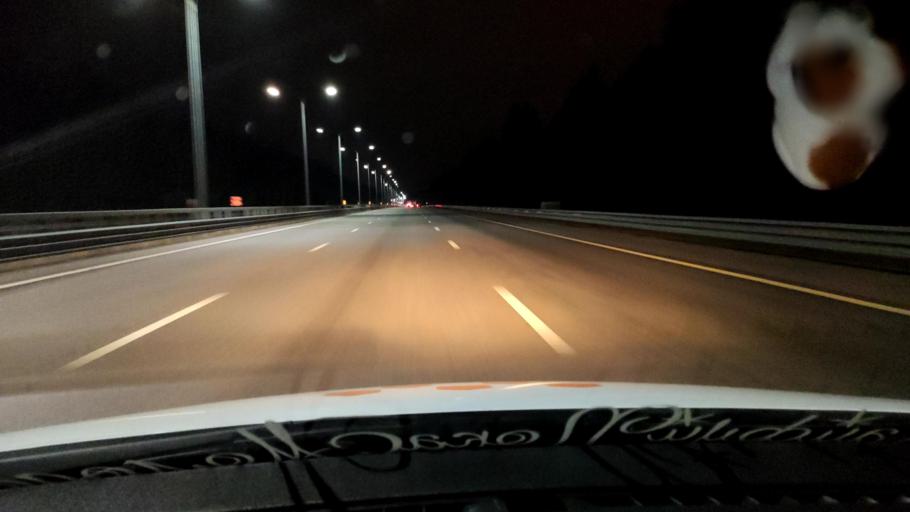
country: RU
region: Voronezj
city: Somovo
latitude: 51.7227
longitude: 39.3101
